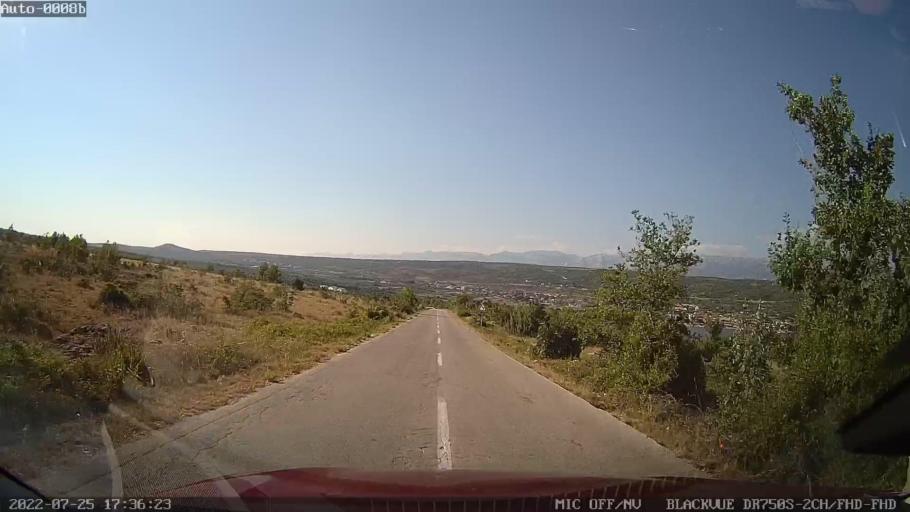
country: HR
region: Zadarska
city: Posedarje
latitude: 44.2001
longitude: 15.4718
